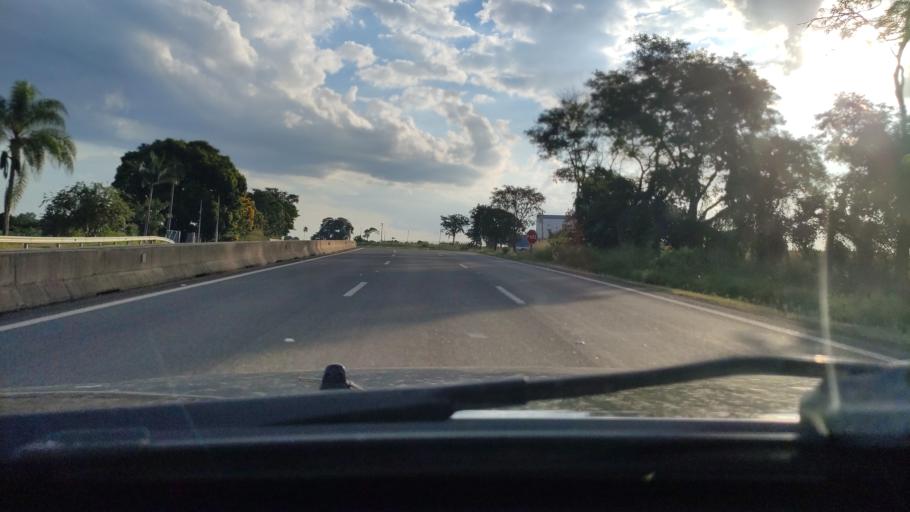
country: BR
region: Sao Paulo
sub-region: Mogi-Mirim
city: Mogi Mirim
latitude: -22.4510
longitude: -47.0842
